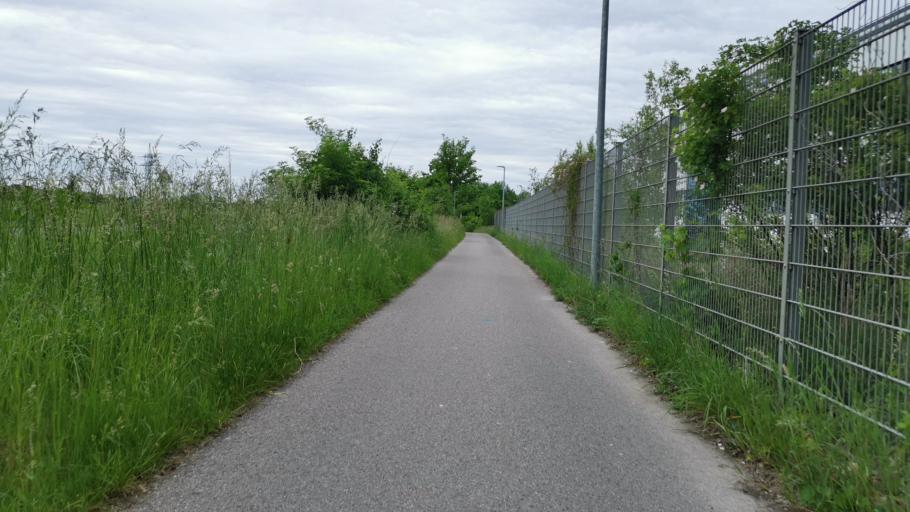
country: DE
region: Bavaria
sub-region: Upper Bavaria
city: Neuried
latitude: 48.1017
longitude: 11.4461
